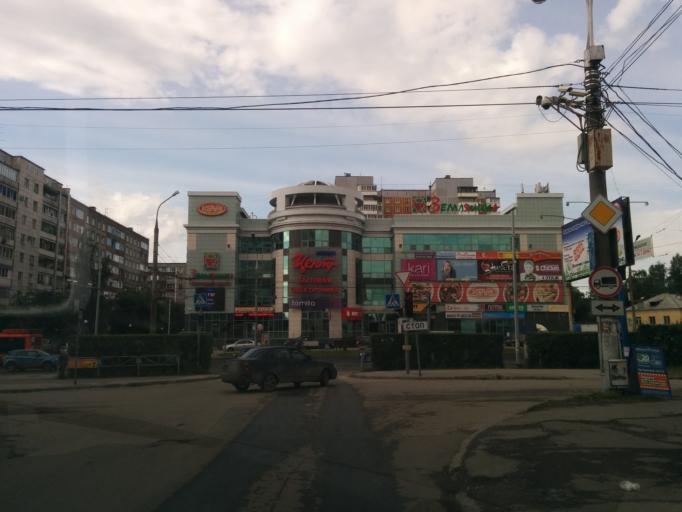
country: RU
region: Perm
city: Kondratovo
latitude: 57.9981
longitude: 56.1555
